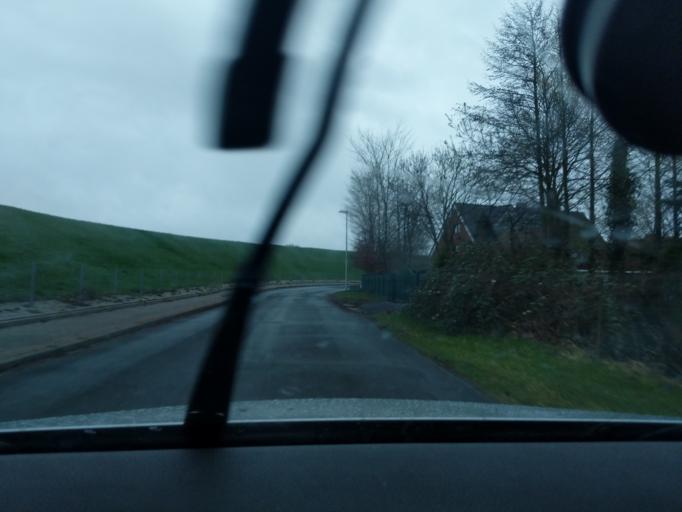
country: DE
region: Schleswig-Holstein
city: Haseldorf
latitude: 53.5882
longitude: 9.5847
